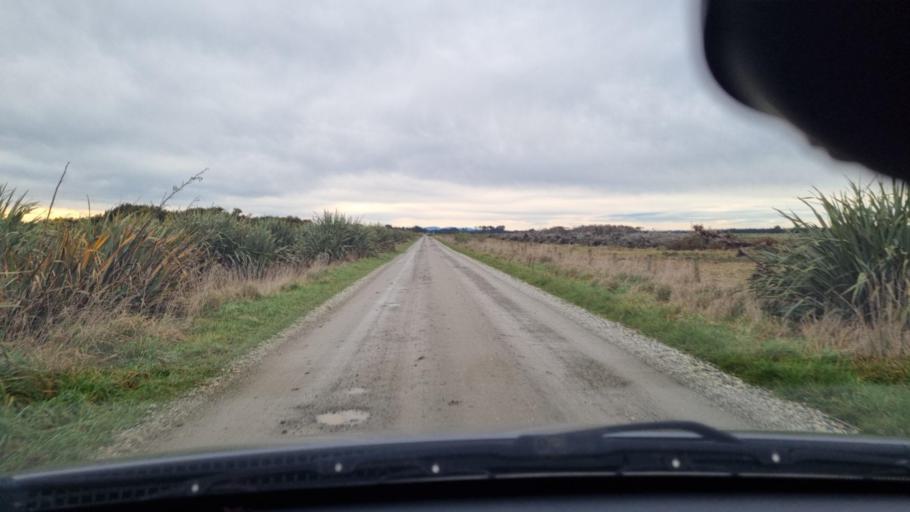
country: NZ
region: Southland
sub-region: Invercargill City
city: Invercargill
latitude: -46.3969
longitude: 168.2666
